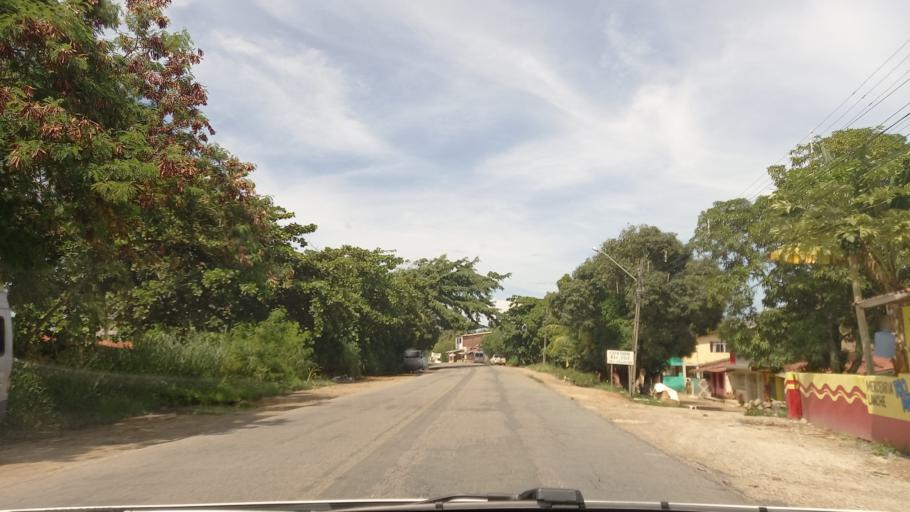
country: BR
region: Pernambuco
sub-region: Sao Jose Da Coroa Grande
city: Sao Jose da Coroa Grande
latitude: -8.9122
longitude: -35.1538
